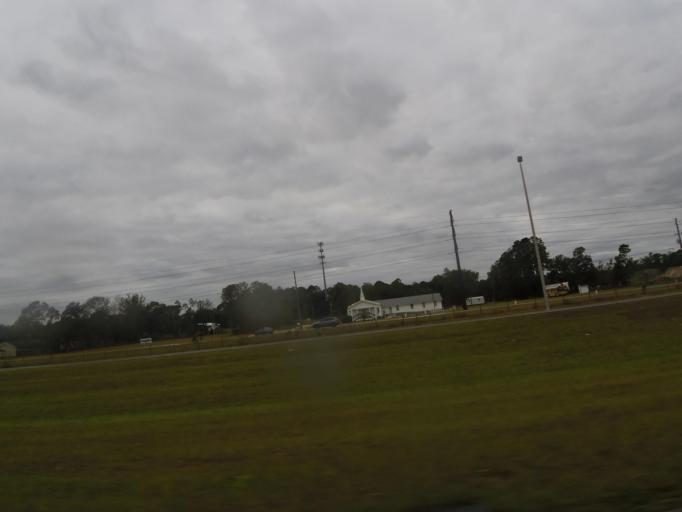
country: US
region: Florida
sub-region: Clay County
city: Lakeside
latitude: 30.1511
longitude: -81.8308
